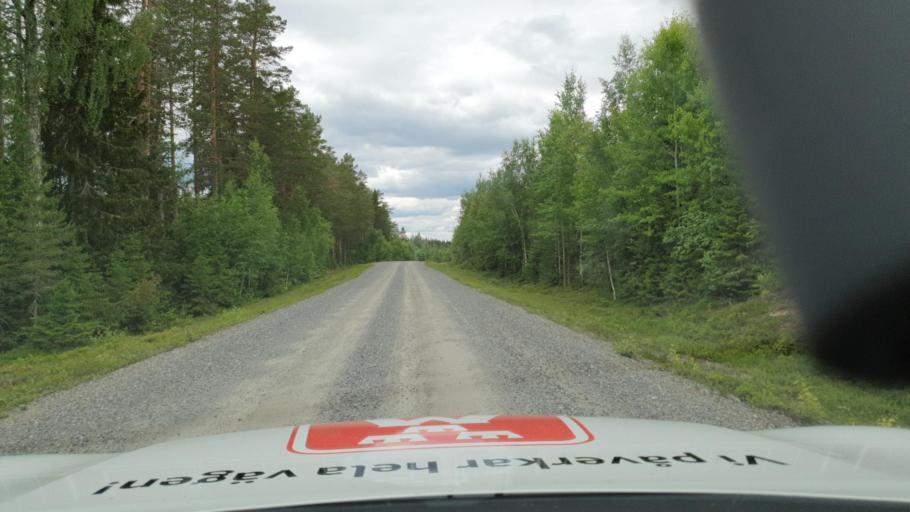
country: SE
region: Vaesterbotten
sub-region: Nordmalings Kommun
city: Nordmaling
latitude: 63.7463
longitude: 19.3797
